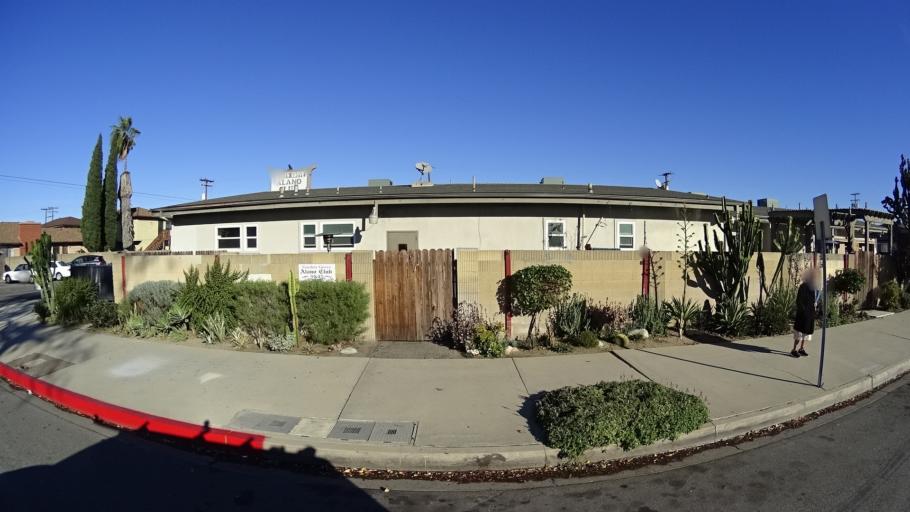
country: US
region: California
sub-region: Orange County
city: Garden Grove
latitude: 33.7721
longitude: -117.9608
